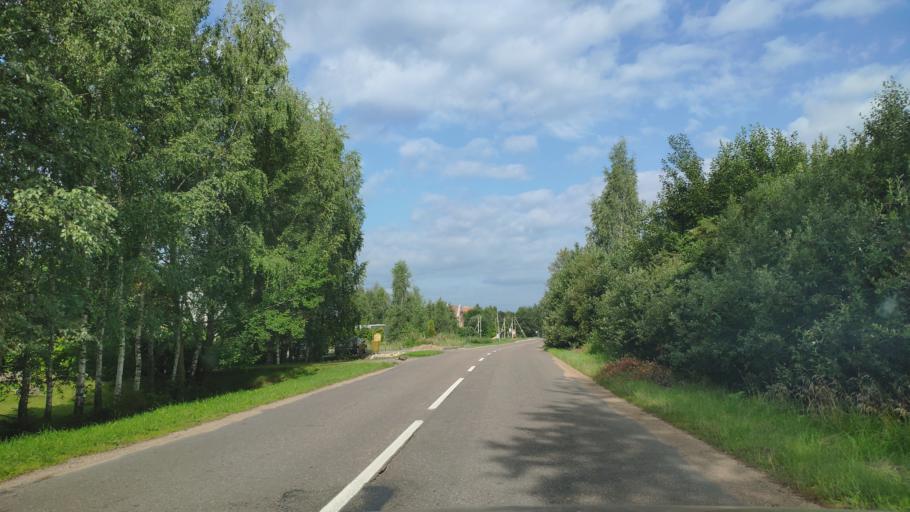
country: BY
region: Minsk
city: Khatsyezhyna
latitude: 53.8739
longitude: 27.2990
